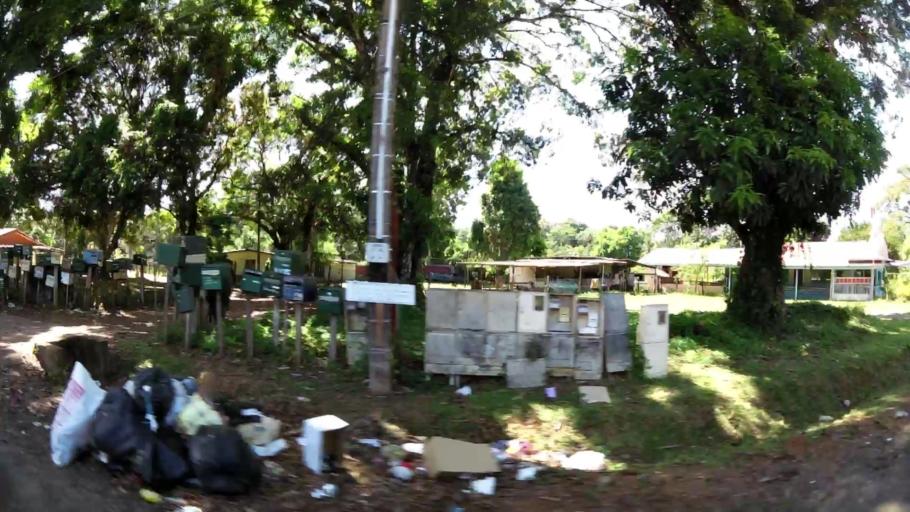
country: GF
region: Guyane
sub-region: Guyane
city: Matoury
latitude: 4.8371
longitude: -52.3269
